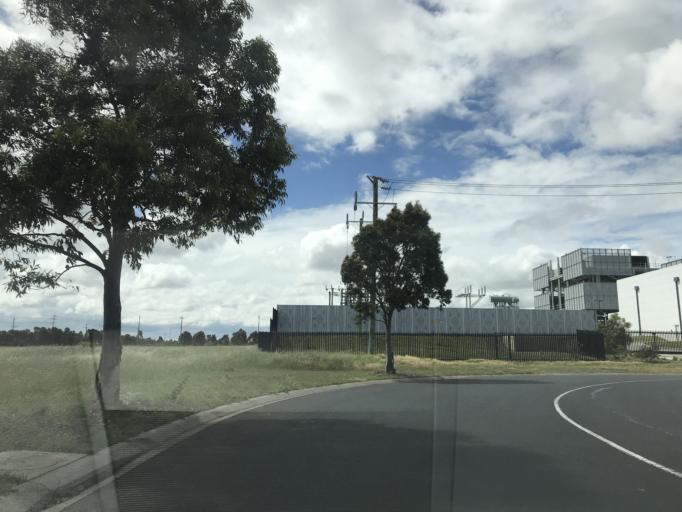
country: AU
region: Victoria
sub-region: Brimbank
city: Derrimut
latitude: -37.8018
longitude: 144.7724
